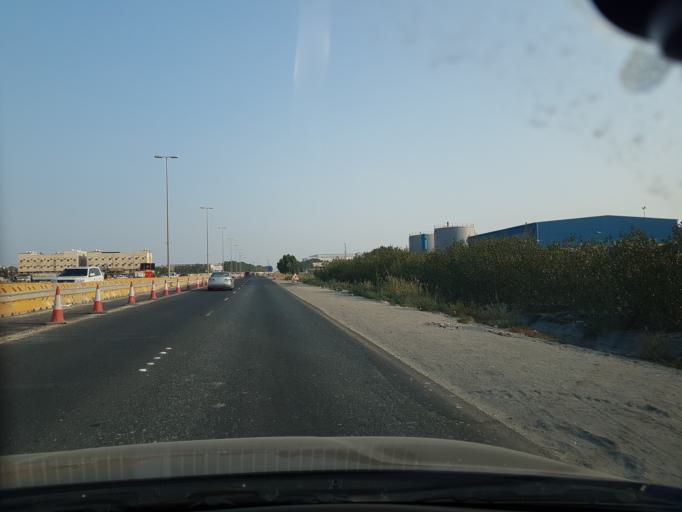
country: BH
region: Northern
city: Sitrah
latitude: 26.0890
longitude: 50.6107
